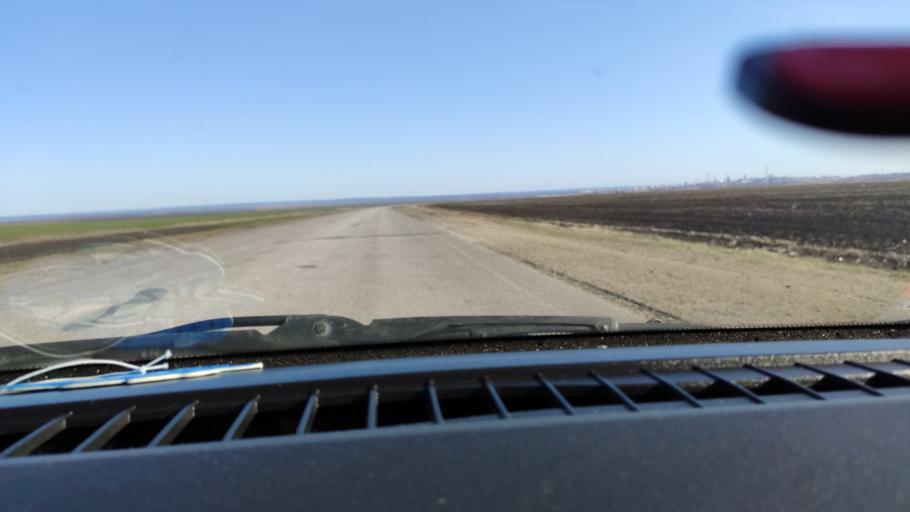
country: RU
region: Samara
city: Varlamovo
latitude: 53.0237
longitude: 48.3336
